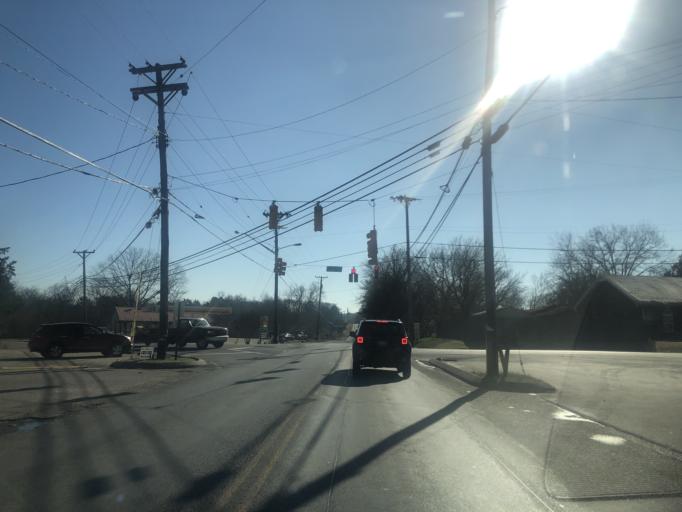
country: US
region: Tennessee
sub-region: Rutherford County
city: La Vergne
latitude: 36.0065
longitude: -86.5669
